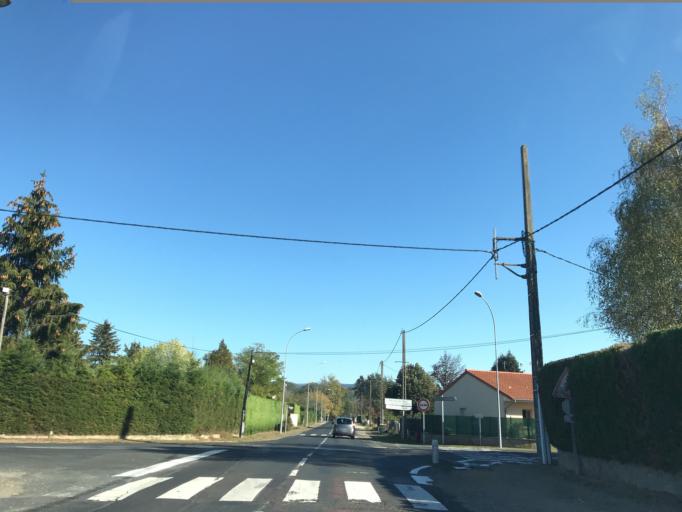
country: FR
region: Auvergne
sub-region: Departement du Puy-de-Dome
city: Courpiere
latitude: 45.7659
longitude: 3.5348
